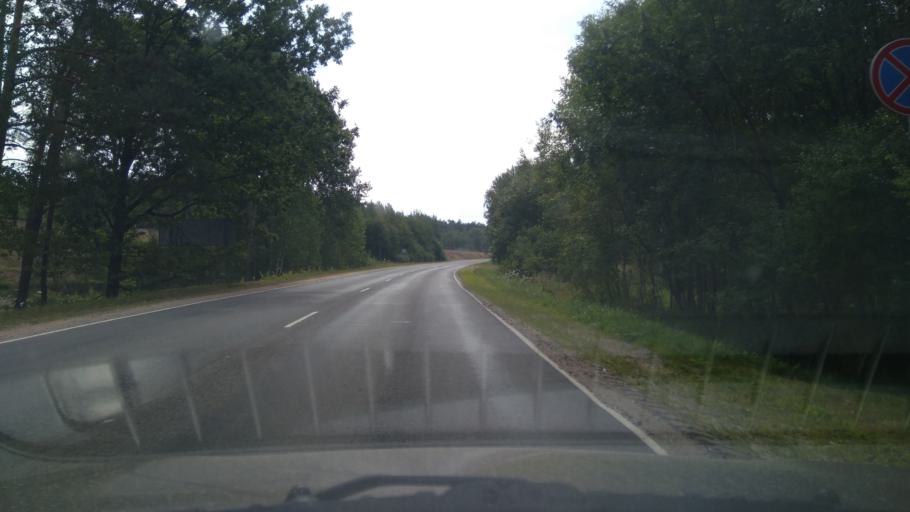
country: BY
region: Brest
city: Nyakhachava
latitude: 52.5864
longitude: 25.0962
